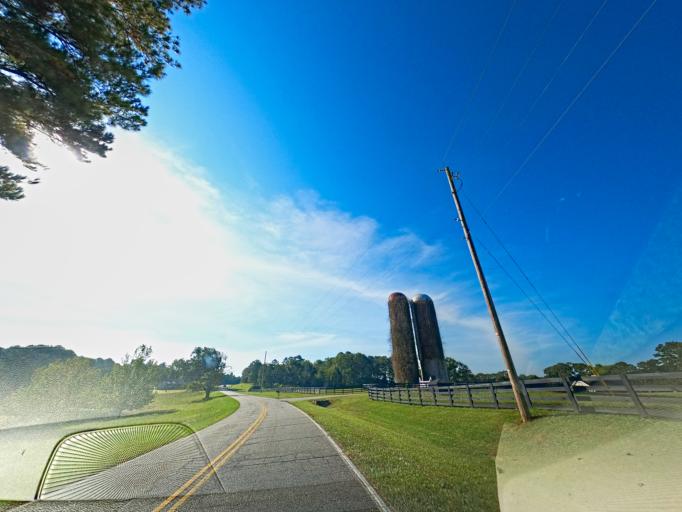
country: US
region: Georgia
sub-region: Coweta County
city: Grantville
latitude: 33.2925
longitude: -84.9309
